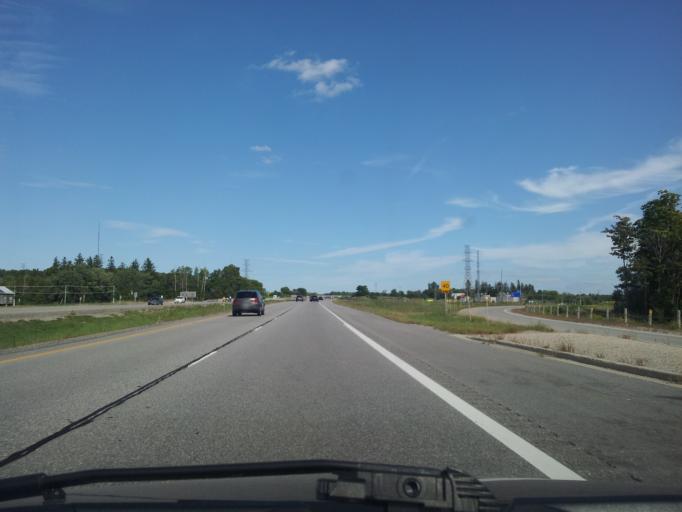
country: CA
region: Ontario
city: Kitchener
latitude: 43.3927
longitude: -80.6599
